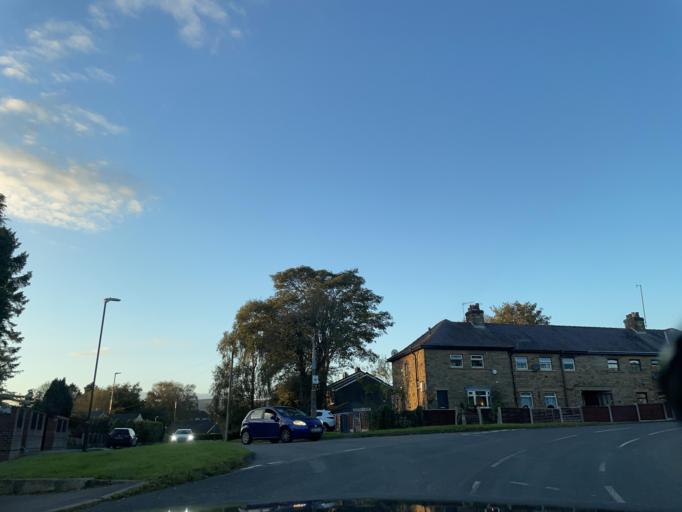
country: GB
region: England
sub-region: Borough of Tameside
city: Longdendale
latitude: 53.4547
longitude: -1.9772
